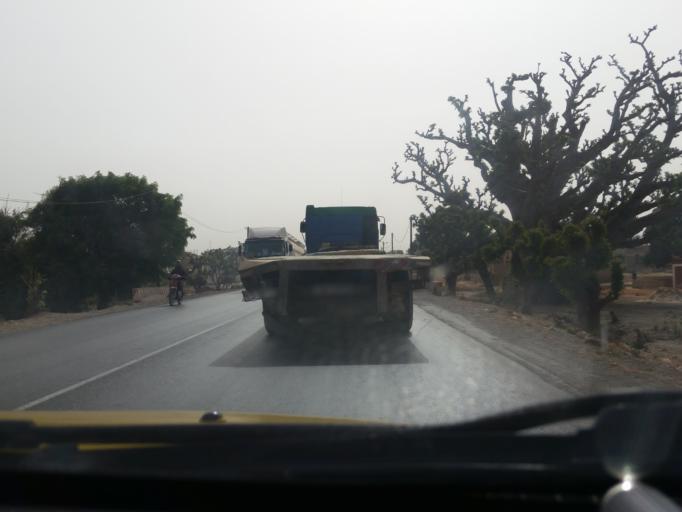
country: SN
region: Thies
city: Pout
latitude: 14.7350
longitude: -17.1516
